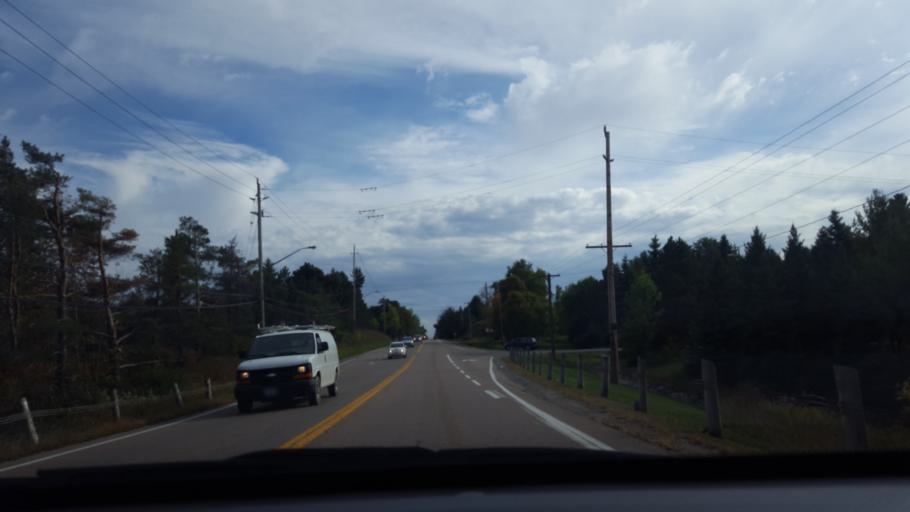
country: CA
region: Ontario
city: Vaughan
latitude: 43.9171
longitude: -79.5527
